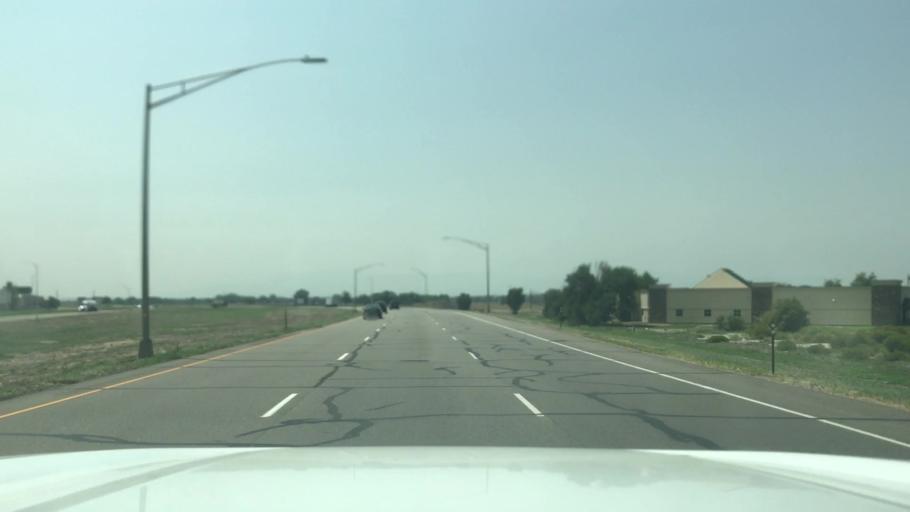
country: US
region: Colorado
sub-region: Pueblo County
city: Pueblo
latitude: 38.2154
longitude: -104.6235
